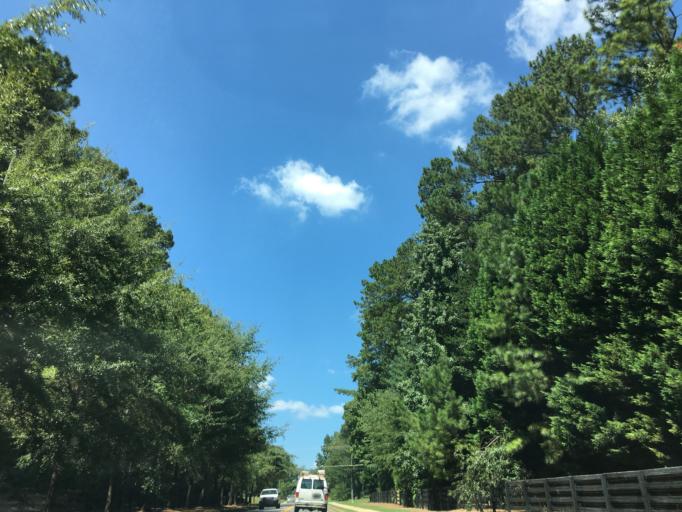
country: US
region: Georgia
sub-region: Fulton County
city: Milton
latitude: 34.1191
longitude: -84.3285
